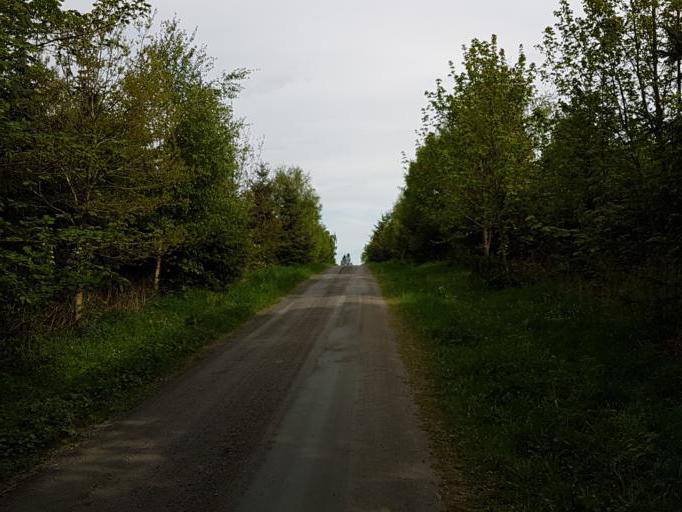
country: SE
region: Skane
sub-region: Lunds Kommun
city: Veberod
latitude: 55.6025
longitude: 13.5193
